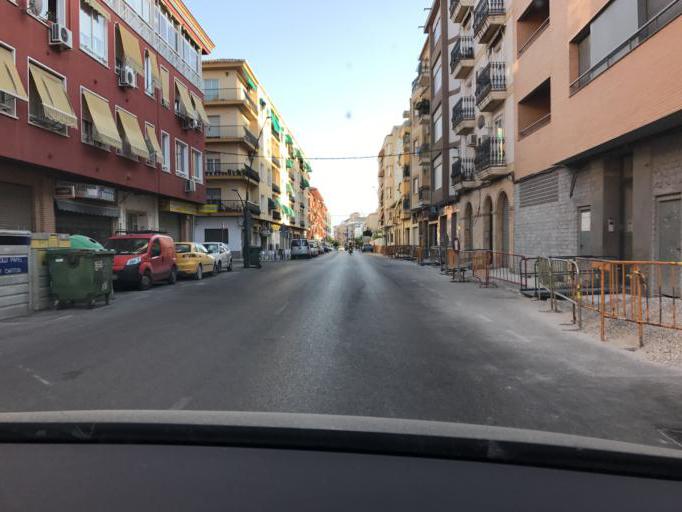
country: ES
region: Andalusia
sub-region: Provincia de Jaen
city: Ubeda
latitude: 38.0188
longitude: -3.3710
